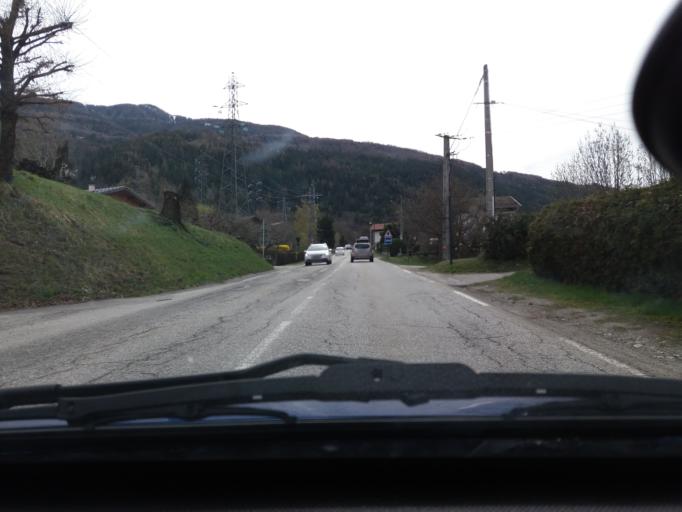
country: FR
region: Rhone-Alpes
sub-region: Departement de la Savoie
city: Macot-la-Plagne
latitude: 45.5543
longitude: 6.6603
